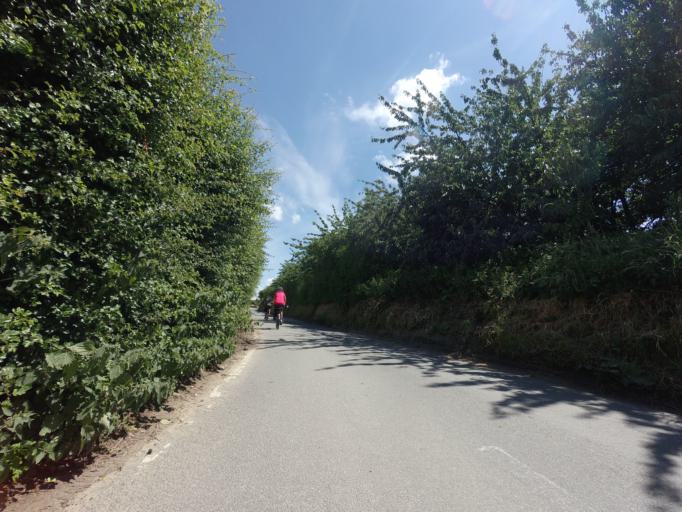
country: GB
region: England
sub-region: Medway
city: Cooling
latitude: 51.4543
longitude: 0.5398
